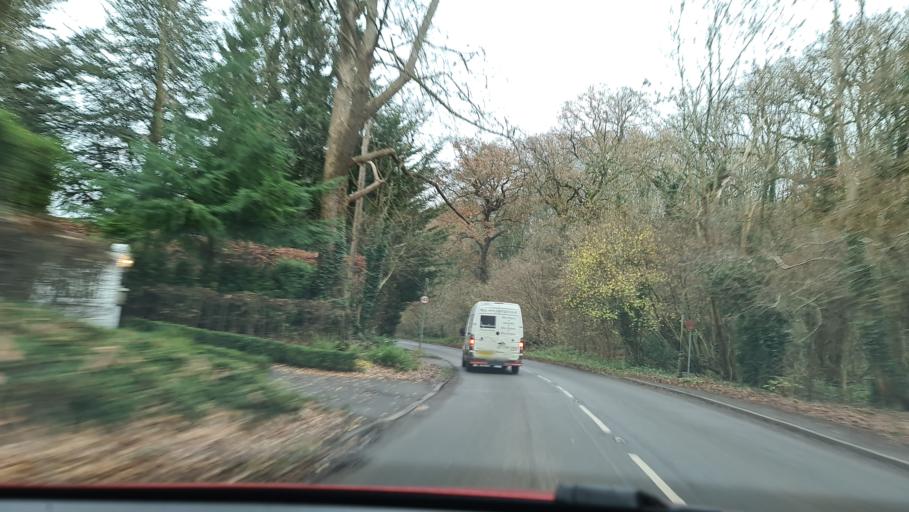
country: GB
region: England
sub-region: Buckinghamshire
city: Seer Green
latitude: 51.6115
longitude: -0.6096
